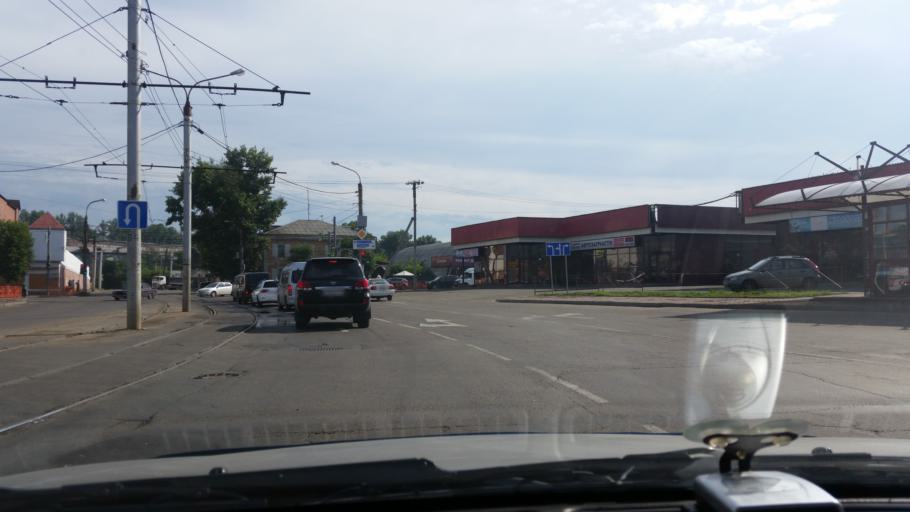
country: RU
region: Irkutsk
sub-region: Irkutskiy Rayon
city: Irkutsk
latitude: 52.2926
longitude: 104.3131
